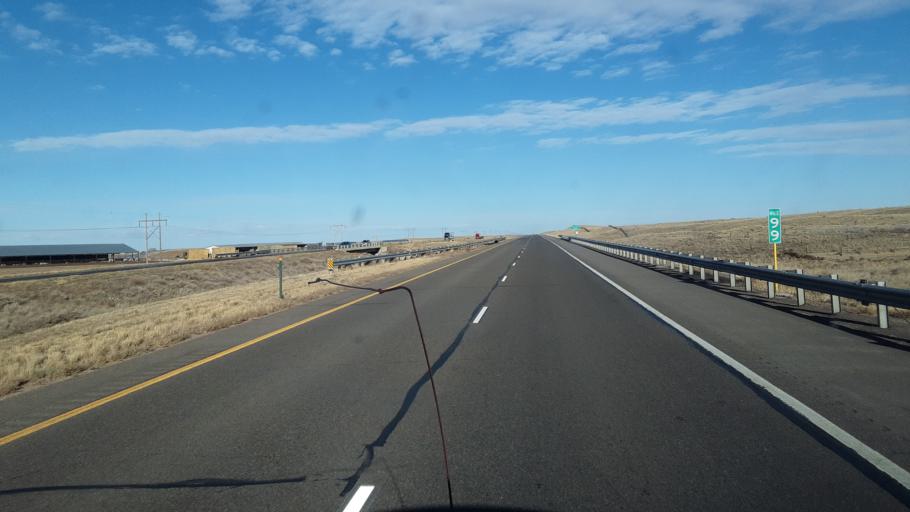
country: US
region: Colorado
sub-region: Morgan County
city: Brush
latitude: 40.3330
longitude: -103.4728
